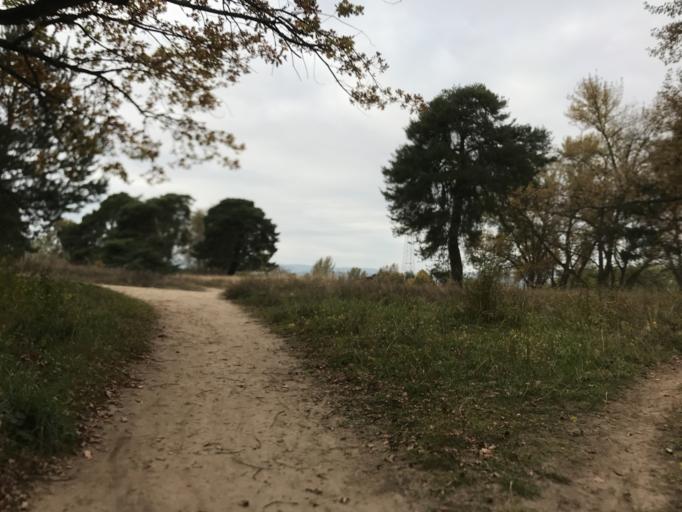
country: DE
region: Rheinland-Pfalz
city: Budenheim
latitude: 50.0173
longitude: 8.2102
